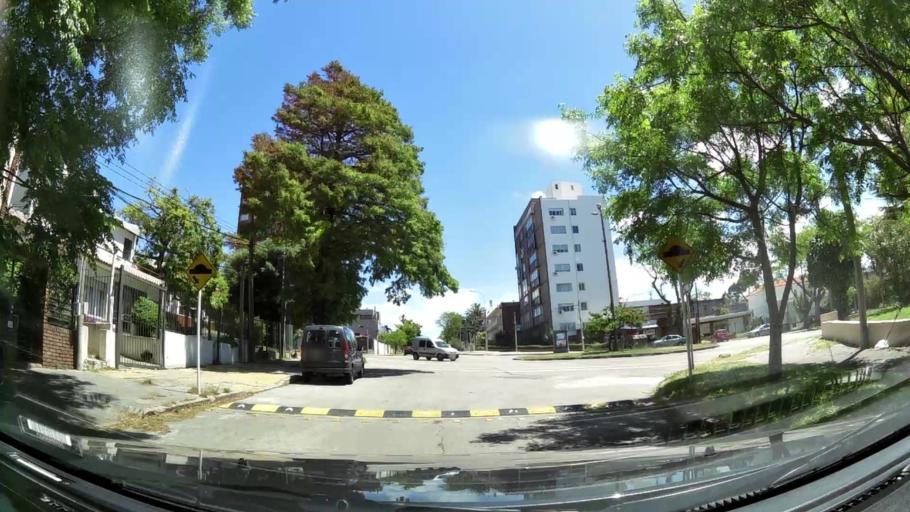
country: UY
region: Canelones
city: Paso de Carrasco
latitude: -34.8944
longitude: -56.1117
